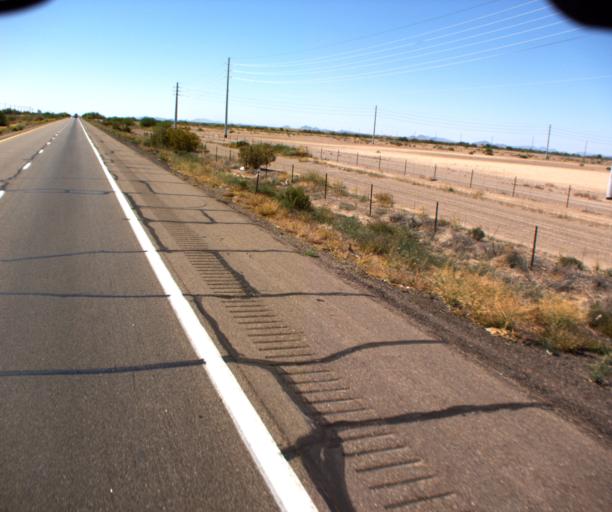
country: US
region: Arizona
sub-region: Maricopa County
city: Gila Bend
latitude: 32.9385
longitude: -112.7645
